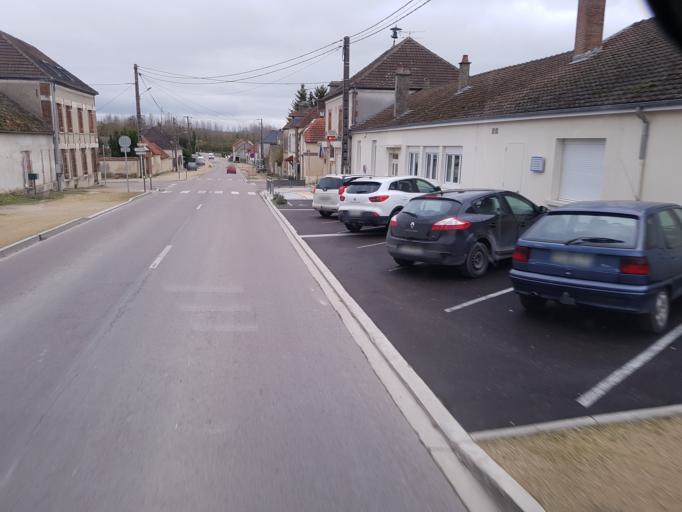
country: FR
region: Champagne-Ardenne
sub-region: Departement de l'Aube
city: Mery-sur-Seine
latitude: 48.4863
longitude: 3.8830
